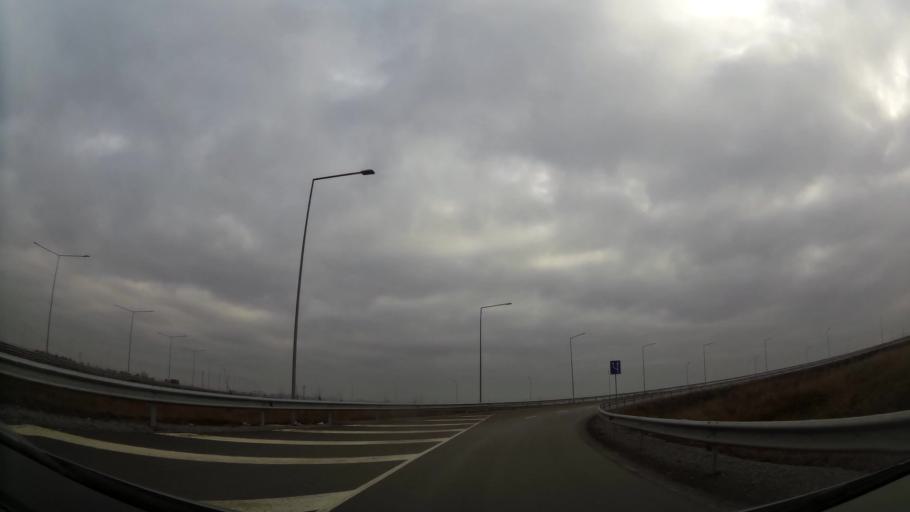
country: BG
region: Sofia-Capital
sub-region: Stolichna Obshtina
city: Sofia
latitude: 42.7698
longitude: 23.2894
